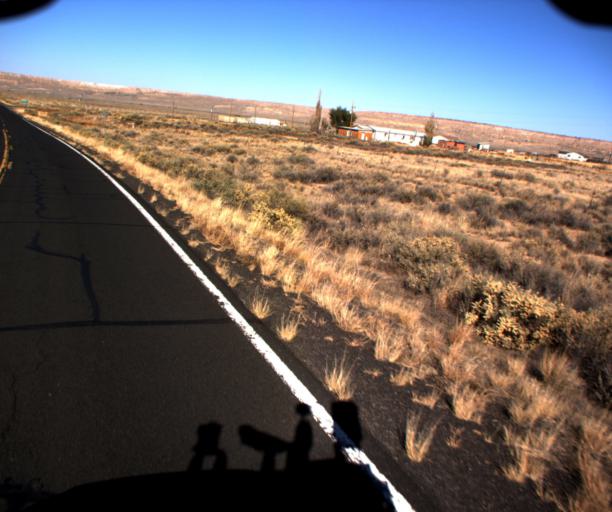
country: US
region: Arizona
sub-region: Navajo County
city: First Mesa
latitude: 35.8388
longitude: -110.3052
